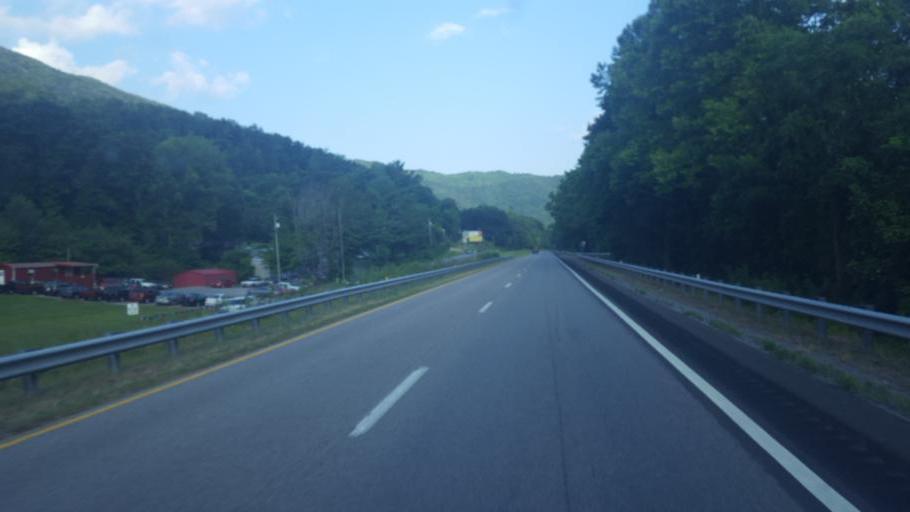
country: US
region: Virginia
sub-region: Lee County
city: Dryden
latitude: 36.7590
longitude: -82.8157
